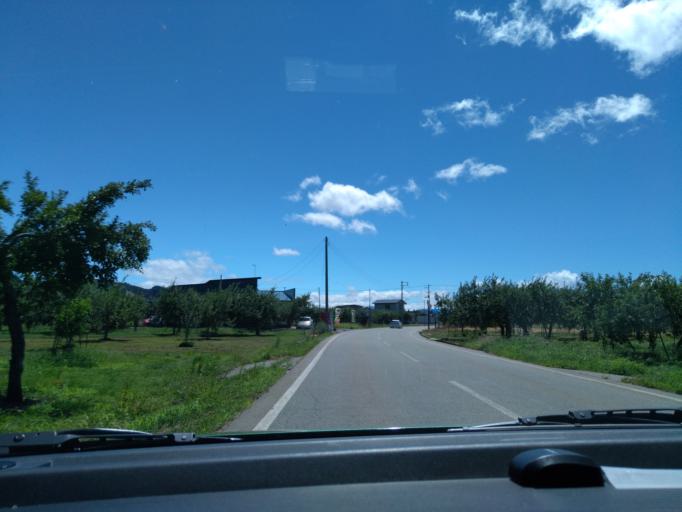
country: JP
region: Akita
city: Yuzawa
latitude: 39.2151
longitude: 140.5662
